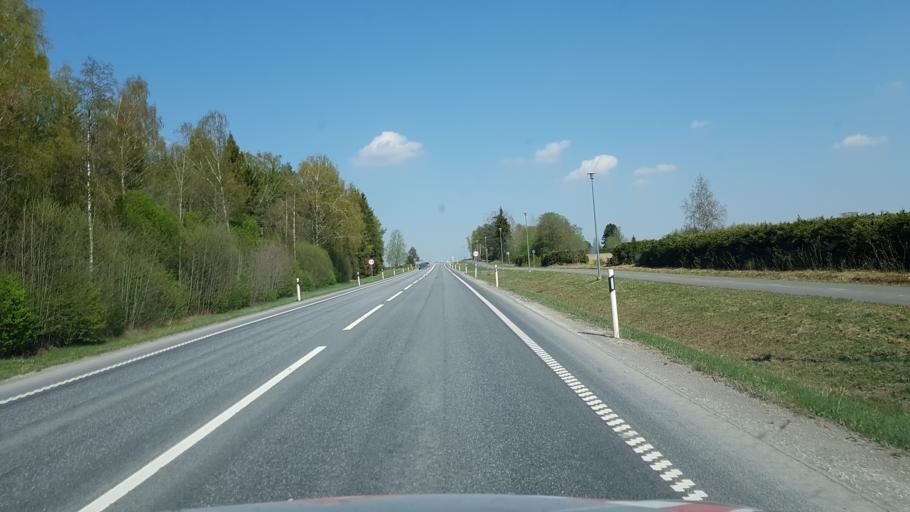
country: EE
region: Jaervamaa
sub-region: Tueri vald
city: Tueri
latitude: 58.8340
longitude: 25.4705
